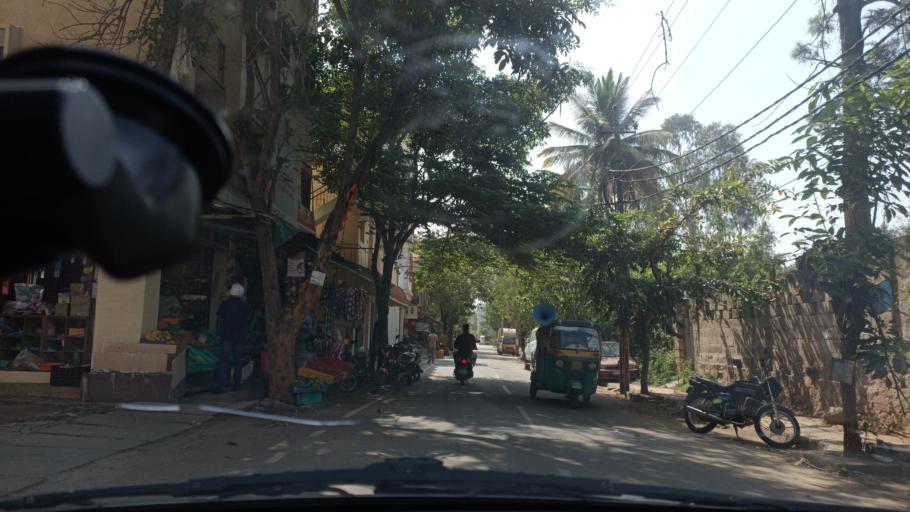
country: IN
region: Karnataka
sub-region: Bangalore Urban
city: Yelahanka
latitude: 13.1100
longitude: 77.6071
